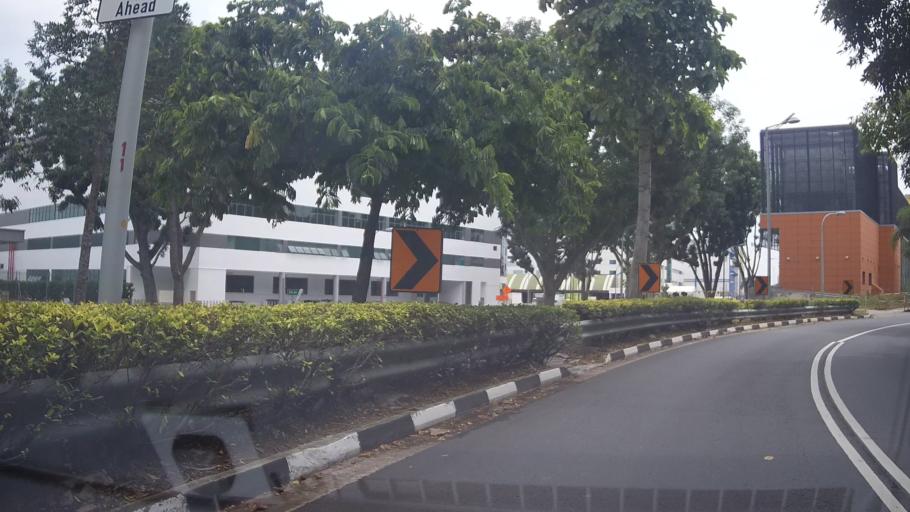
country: SG
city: Singapore
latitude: 1.3332
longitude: 103.9666
